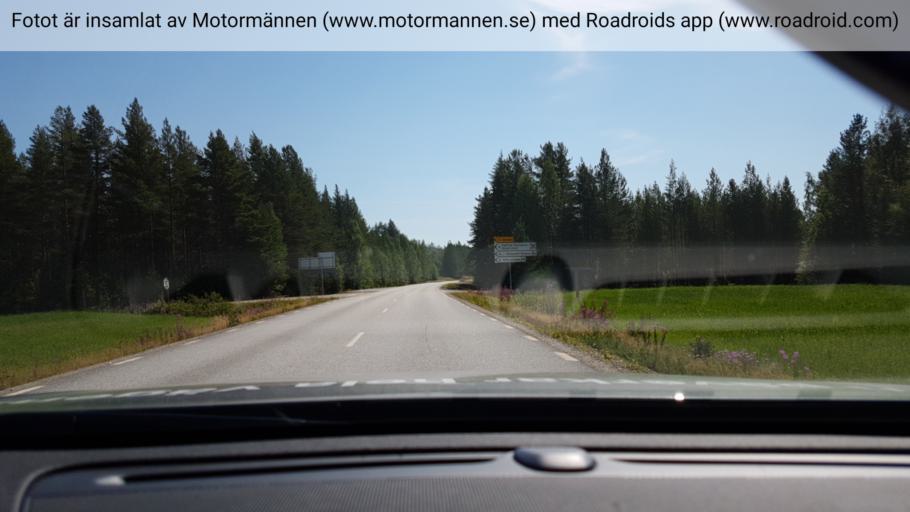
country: SE
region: Vaesterbotten
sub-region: Vindelns Kommun
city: Vindeln
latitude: 64.3621
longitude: 19.4450
